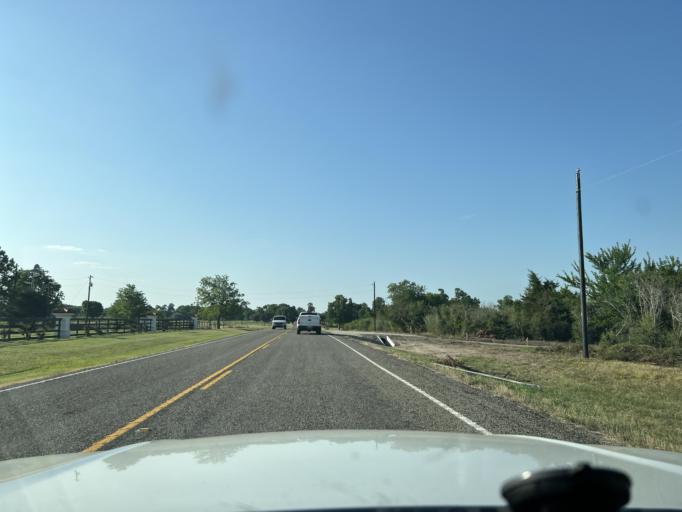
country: US
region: Texas
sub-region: Washington County
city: Brenham
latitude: 30.2243
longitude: -96.2381
